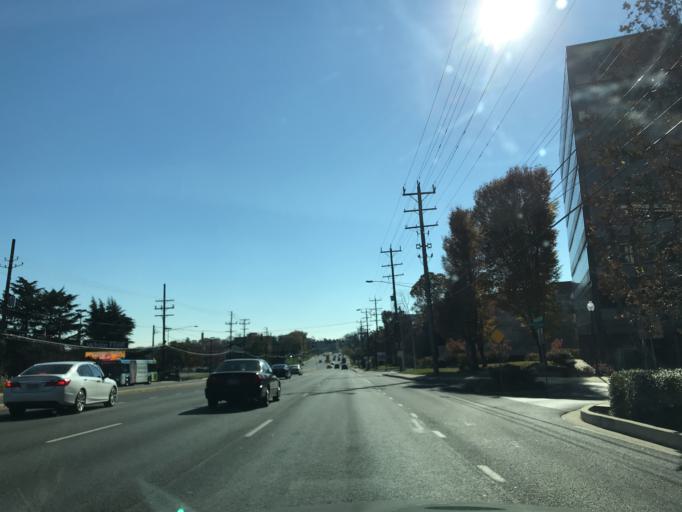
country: US
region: Maryland
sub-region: Montgomery County
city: North Bethesda
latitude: 39.0429
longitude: -77.1110
